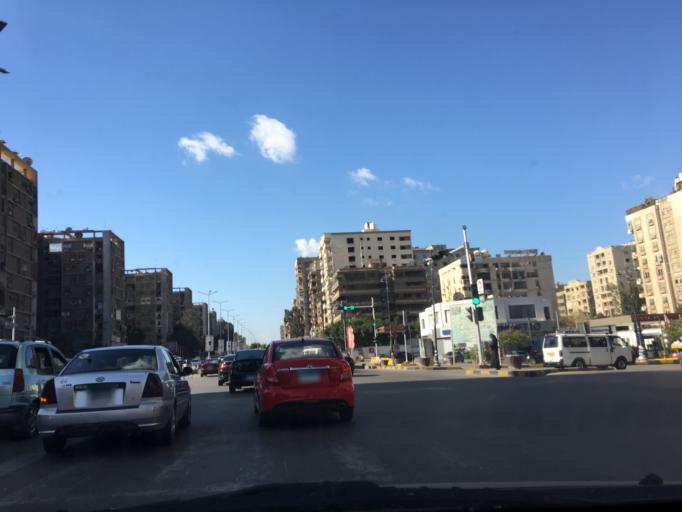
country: EG
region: Muhafazat al Qahirah
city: Cairo
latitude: 30.0539
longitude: 31.3389
